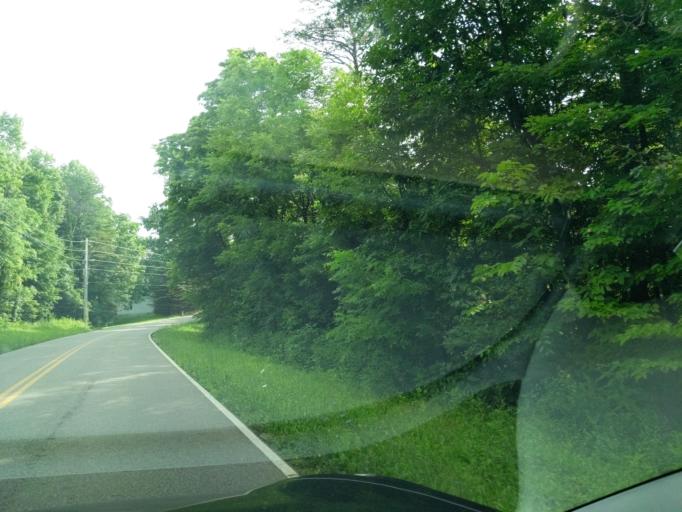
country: US
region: Ohio
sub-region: Fairfield County
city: Lancaster
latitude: 39.5652
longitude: -82.5960
